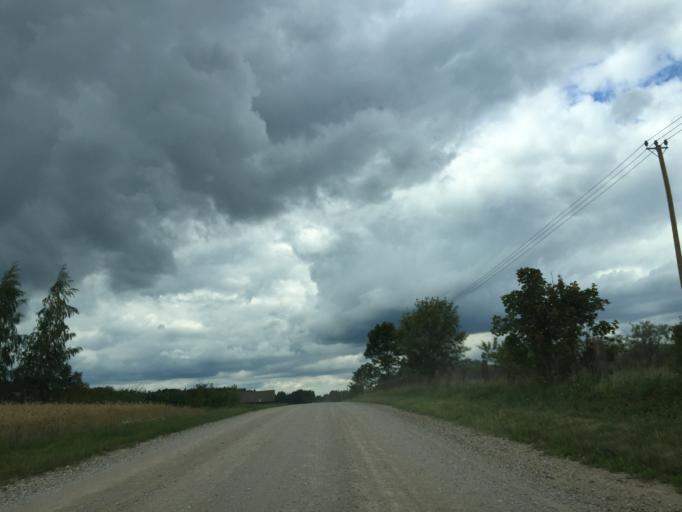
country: LV
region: Malpils
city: Malpils
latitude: 56.8633
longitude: 25.0152
